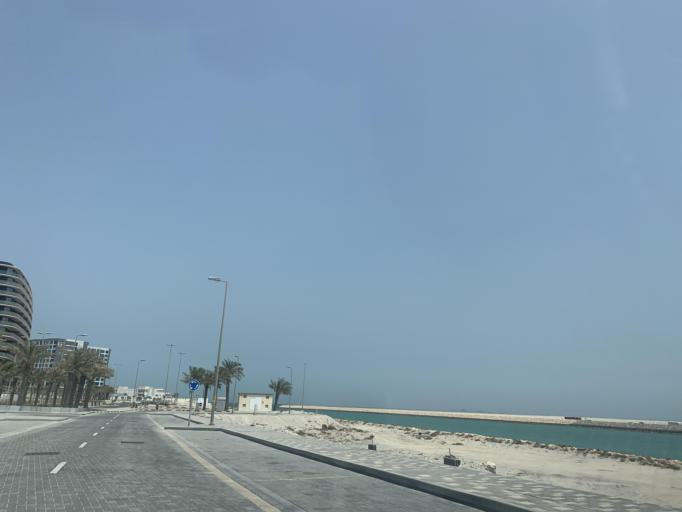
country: BH
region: Muharraq
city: Al Hadd
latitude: 26.2681
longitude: 50.6718
